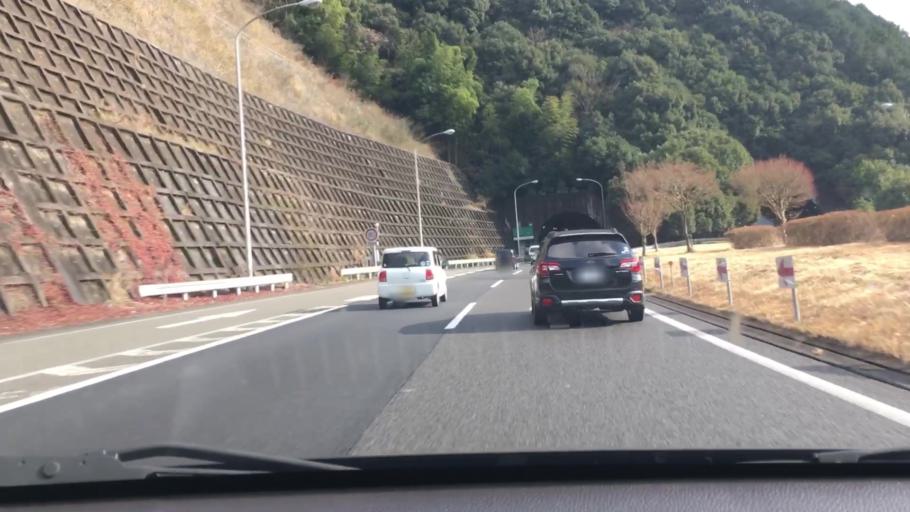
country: JP
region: Kumamoto
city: Yatsushiro
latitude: 32.4416
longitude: 130.6702
